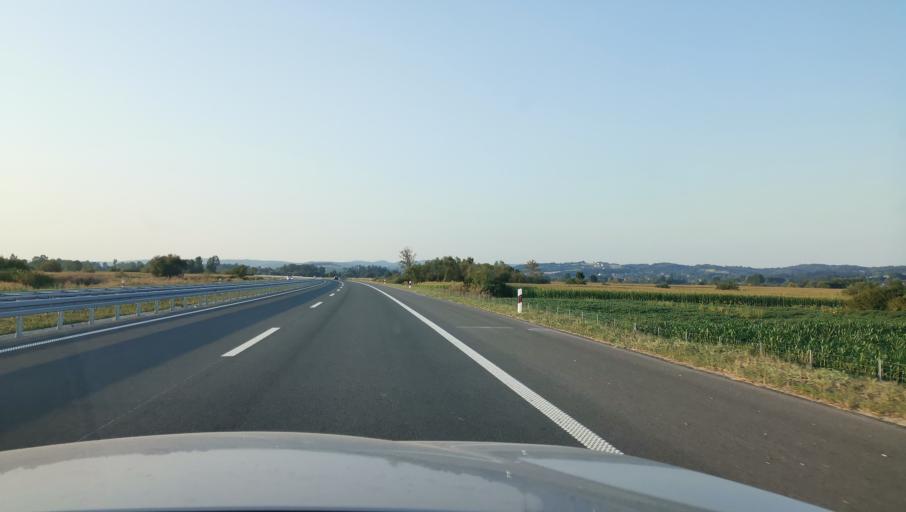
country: RS
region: Central Serbia
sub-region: Kolubarski Okrug
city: Ljig
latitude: 44.2555
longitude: 20.2707
